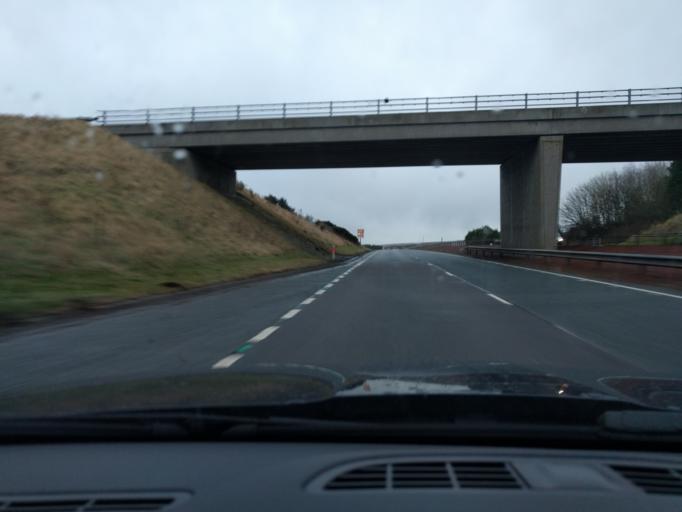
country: GB
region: England
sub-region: Northumberland
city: Berwick-Upon-Tweed
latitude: 55.8113
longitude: -2.0455
